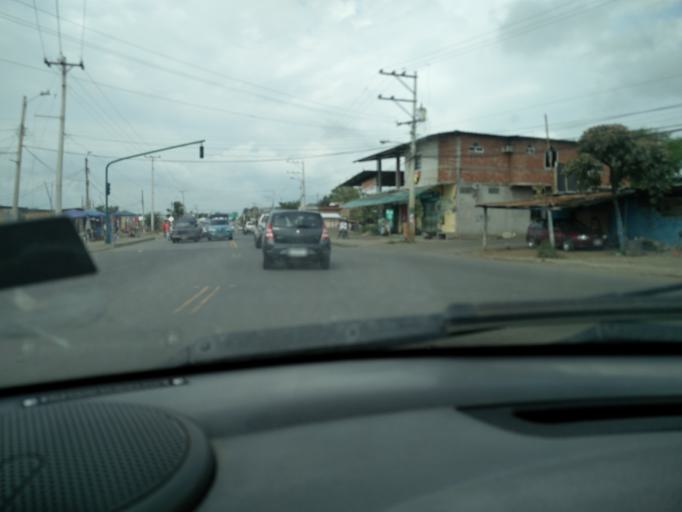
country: EC
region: Manabi
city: Rocafuerte
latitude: -0.9184
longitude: -80.4446
